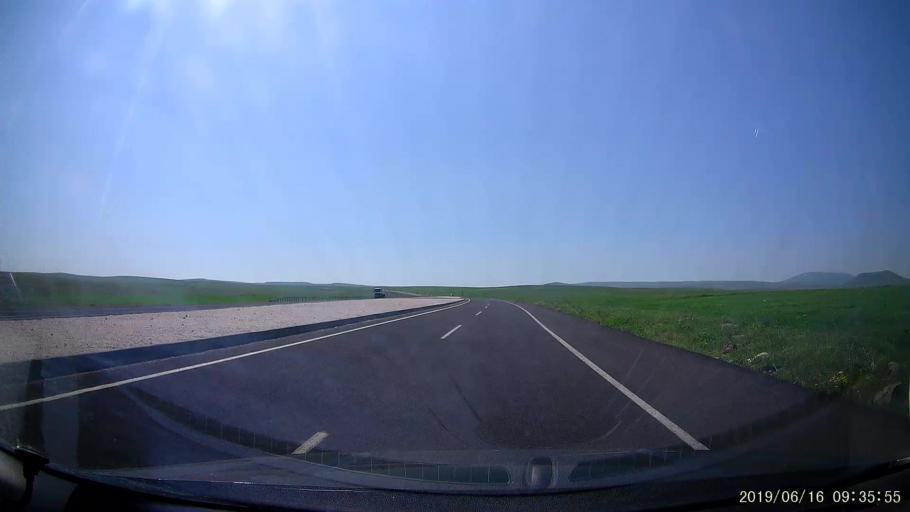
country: TR
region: Kars
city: Kars
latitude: 40.5643
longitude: 43.1639
